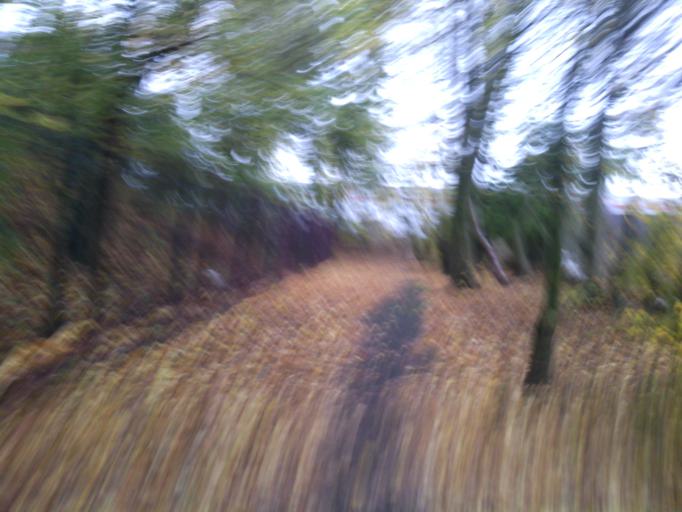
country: BE
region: Wallonia
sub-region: Province du Hainaut
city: Mouscron
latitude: 50.7599
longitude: 3.2237
